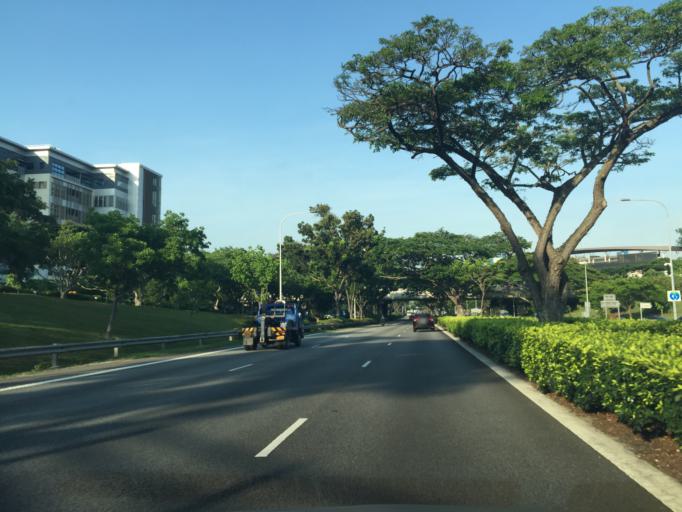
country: SG
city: Singapore
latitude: 1.3425
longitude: 103.9481
